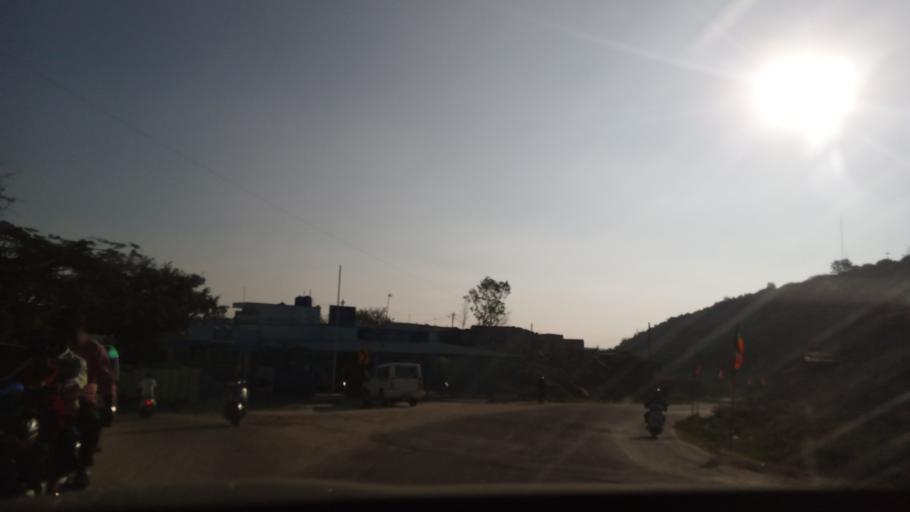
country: IN
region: Tamil Nadu
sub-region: Krishnagiri
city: Hosur
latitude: 12.7266
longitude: 77.8423
